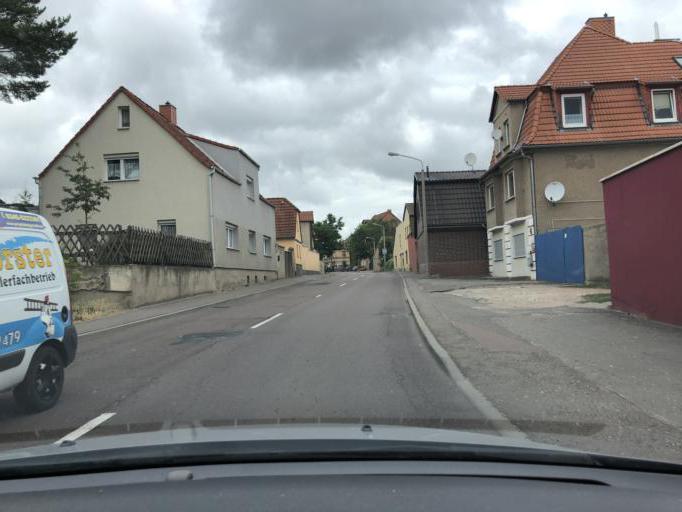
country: DE
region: Saxony-Anhalt
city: Schkopau
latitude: 51.4227
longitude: 11.9947
